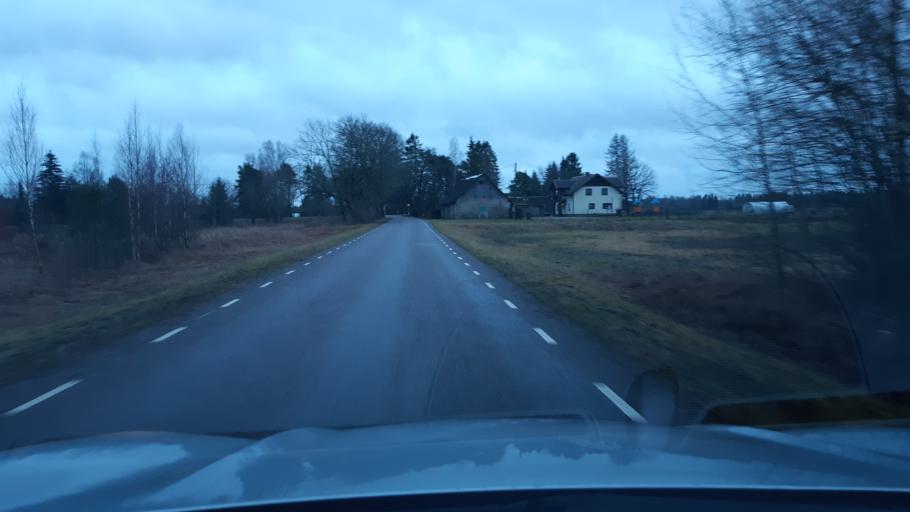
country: EE
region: Raplamaa
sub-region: Rapla vald
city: Rapla
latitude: 58.9825
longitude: 24.7352
